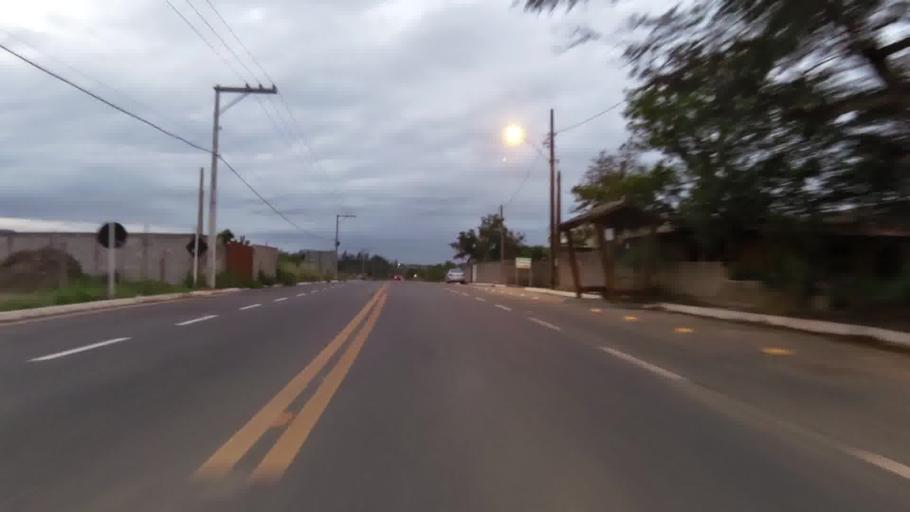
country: BR
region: Espirito Santo
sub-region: Piuma
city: Piuma
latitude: -20.8200
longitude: -40.6170
